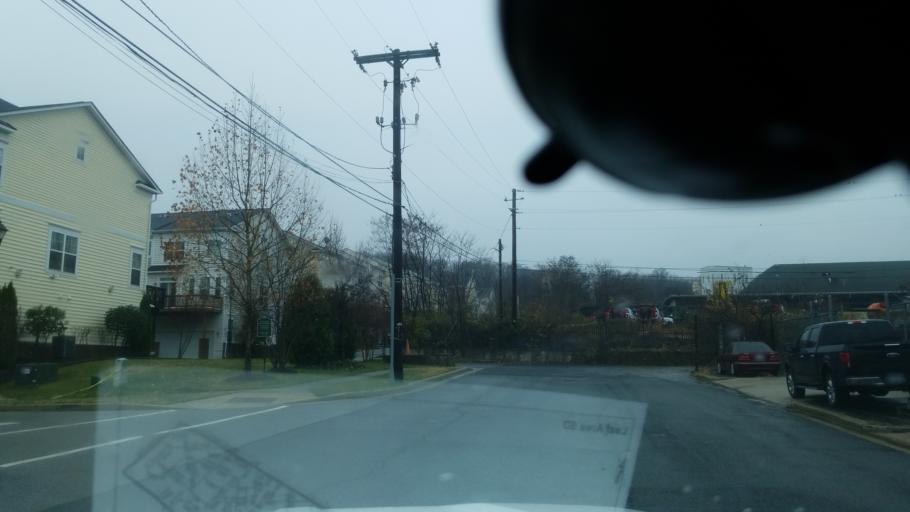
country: US
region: Maryland
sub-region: Prince George's County
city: Chillum
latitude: 38.9501
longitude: -76.9986
